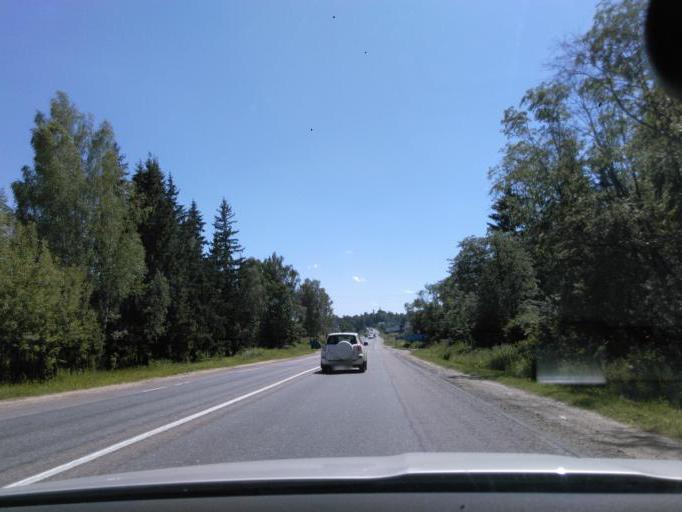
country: RU
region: Moskovskaya
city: Solnechnogorsk
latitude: 56.1581
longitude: 36.9215
